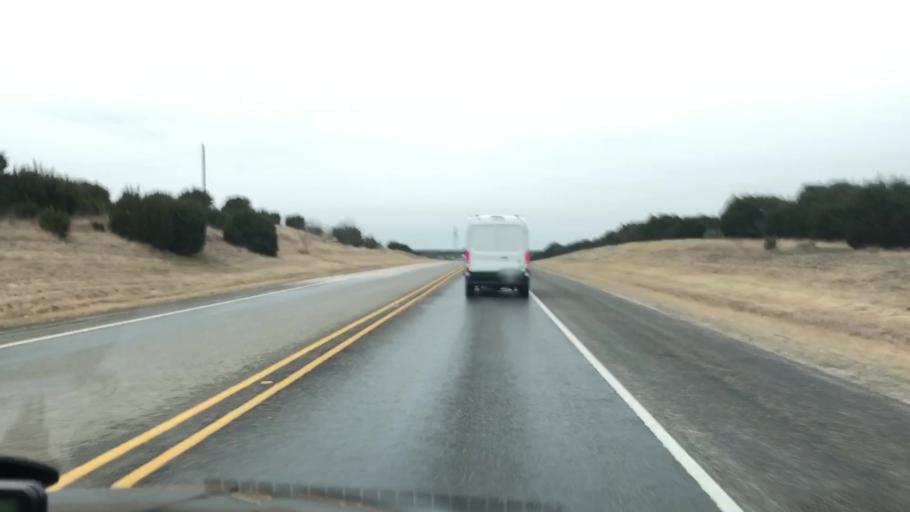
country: US
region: Texas
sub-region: Lampasas County
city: Lampasas
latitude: 31.1329
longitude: -98.1874
